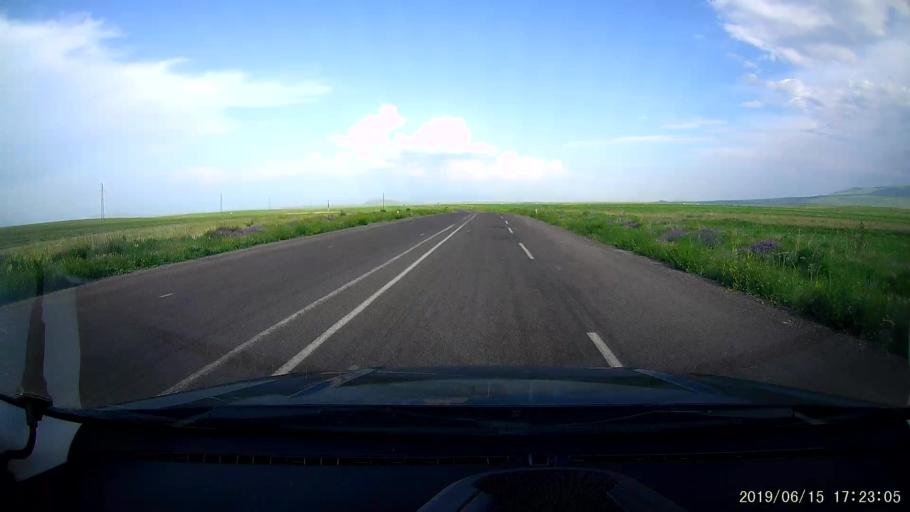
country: TR
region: Kars
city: Basgedikler
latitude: 40.6177
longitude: 43.3549
